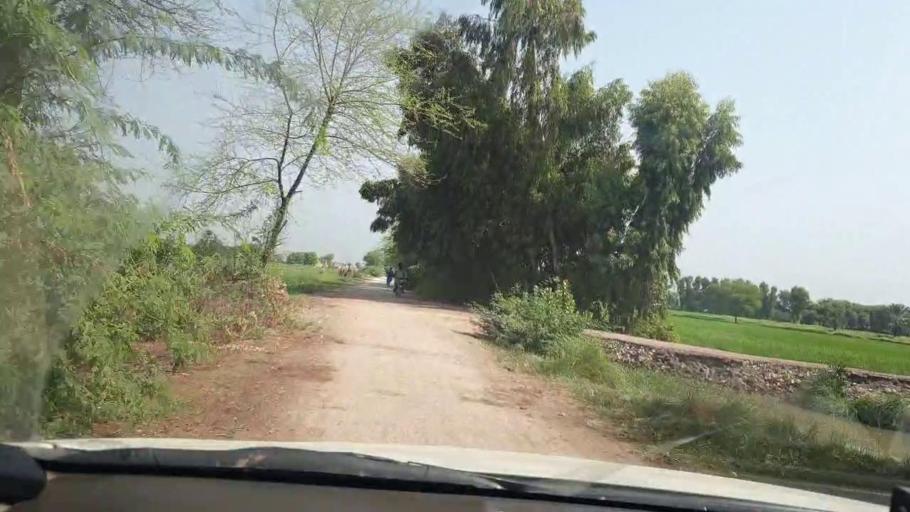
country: PK
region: Sindh
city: Chak
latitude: 27.8303
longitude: 68.7998
